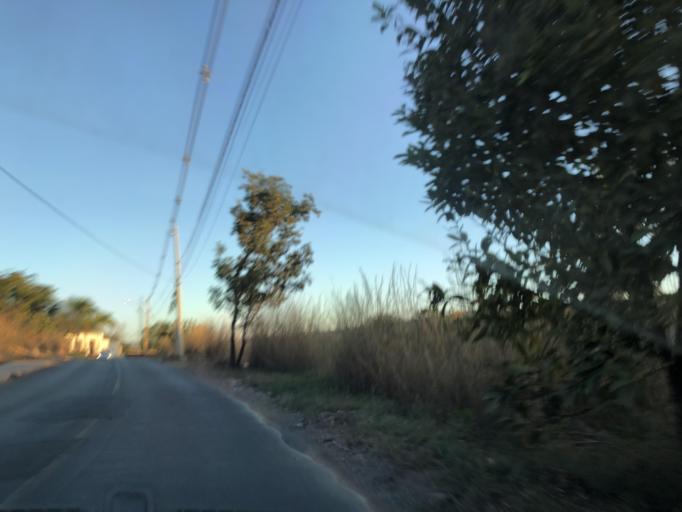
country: BR
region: Federal District
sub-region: Brasilia
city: Brasilia
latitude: -15.8695
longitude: -47.7830
